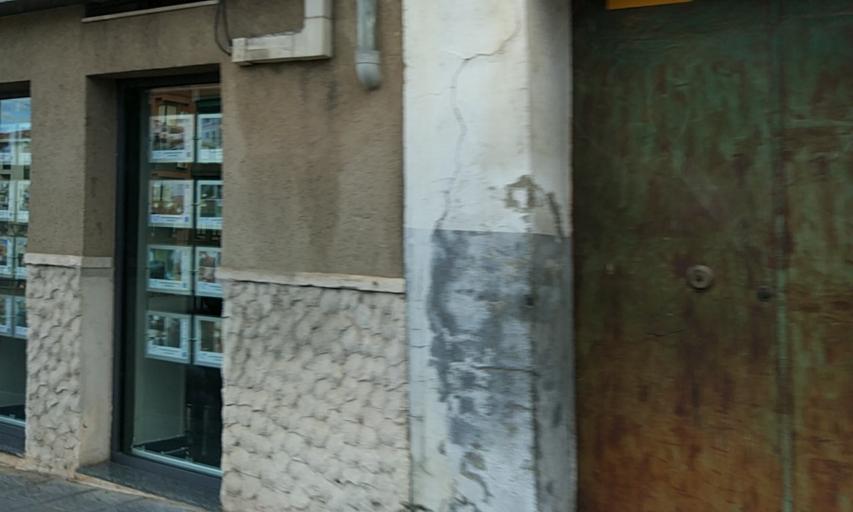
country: ES
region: Extremadura
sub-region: Provincia de Caceres
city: Coria
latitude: 39.9846
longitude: -6.5354
